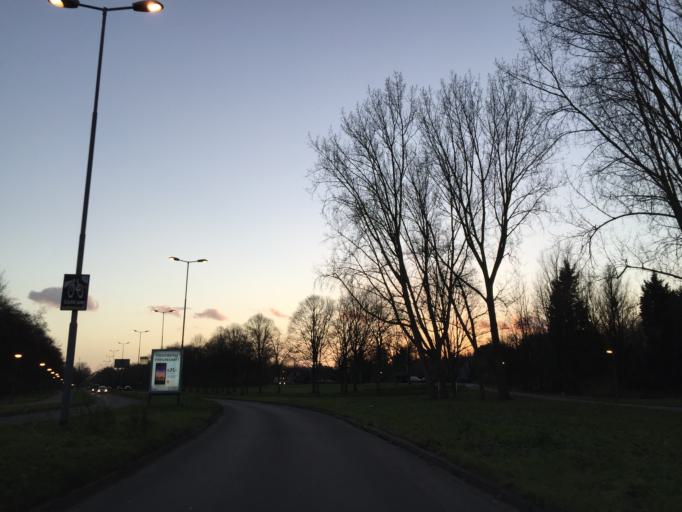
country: NL
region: South Holland
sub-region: Gemeente Lansingerland
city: Bergschenhoek
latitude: 51.9670
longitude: 4.4865
